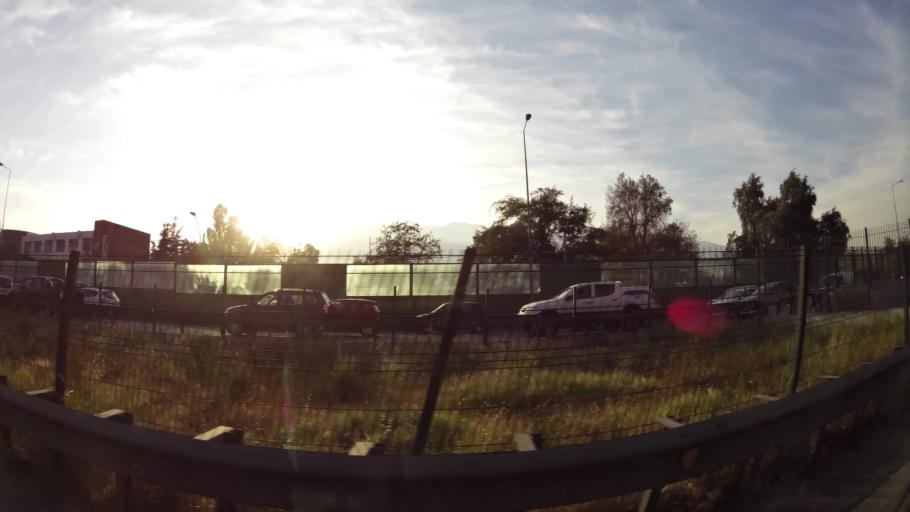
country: CL
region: Santiago Metropolitan
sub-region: Provincia de Santiago
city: Villa Presidente Frei, Nunoa, Santiago, Chile
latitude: -33.4746
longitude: -70.5776
